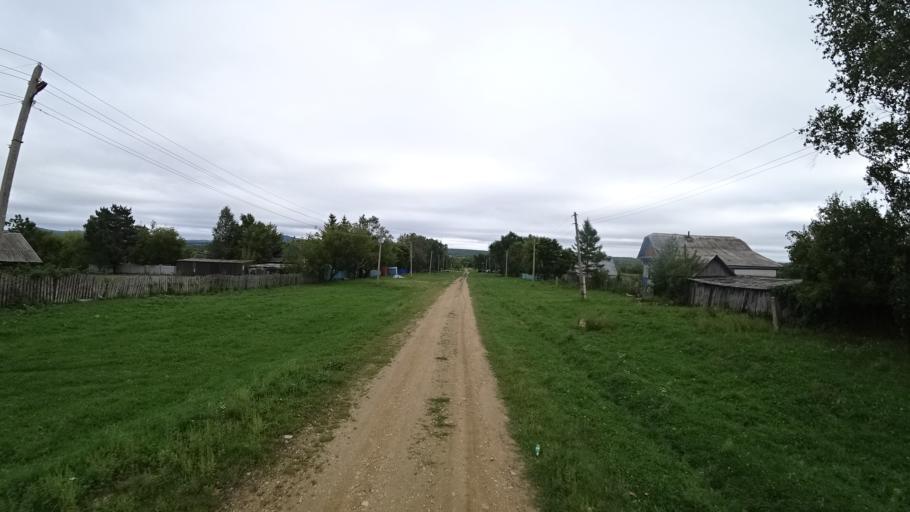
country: RU
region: Primorskiy
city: Rettikhovka
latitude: 44.1386
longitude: 132.6519
